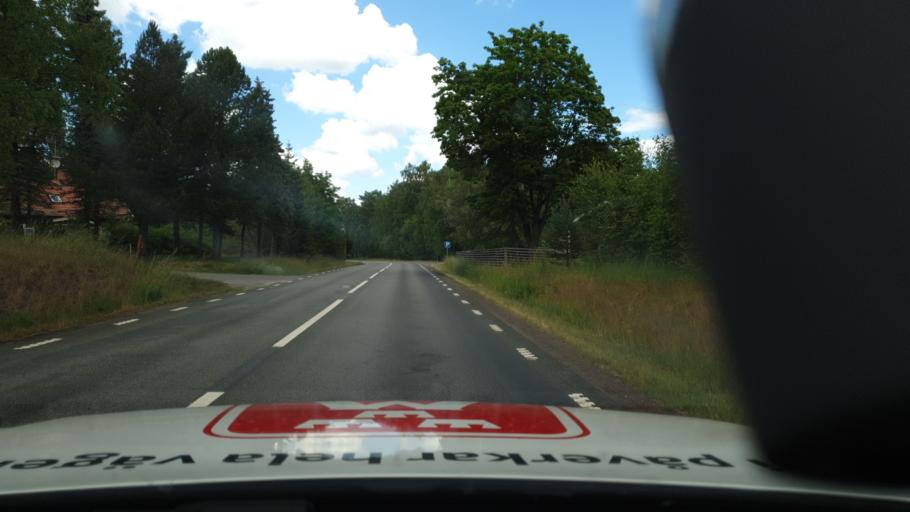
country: SE
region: Vaestra Goetaland
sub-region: Karlsborgs Kommun
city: Molltorp
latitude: 58.4294
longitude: 14.3994
